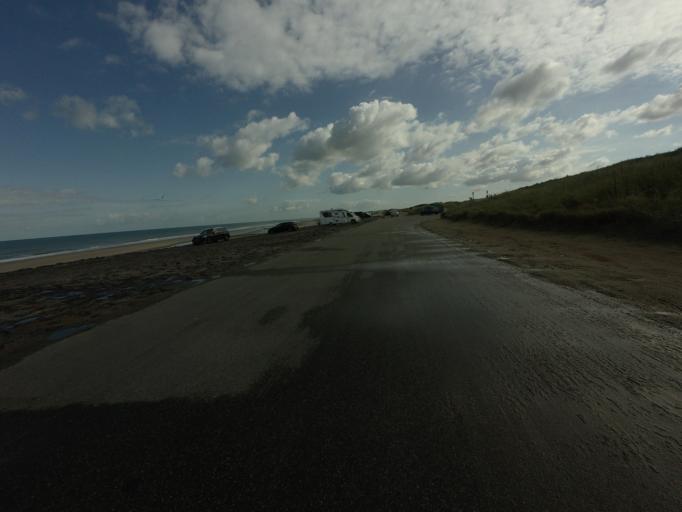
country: NL
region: Zeeland
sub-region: Gemeente Vlissingen
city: Vlissingen
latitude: 51.5484
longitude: 3.4550
